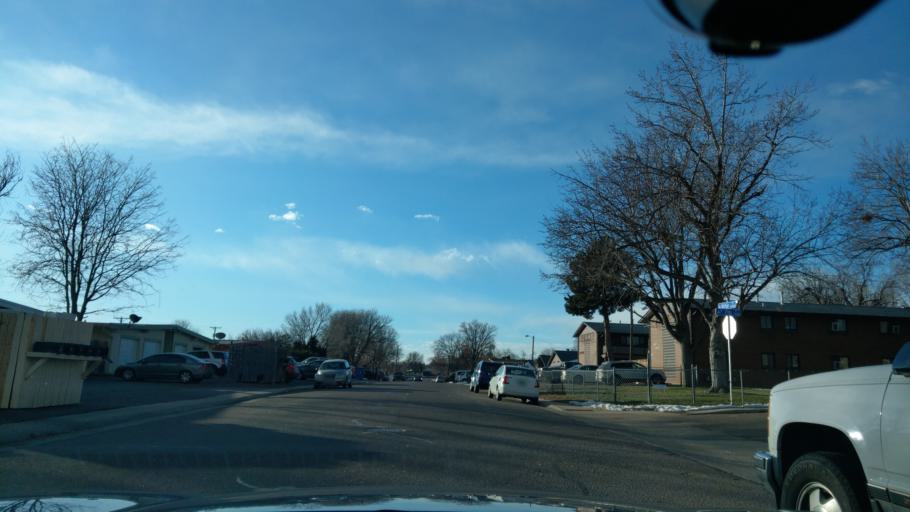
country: US
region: Colorado
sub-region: Jefferson County
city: Lakewood
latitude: 39.7294
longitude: -105.1149
